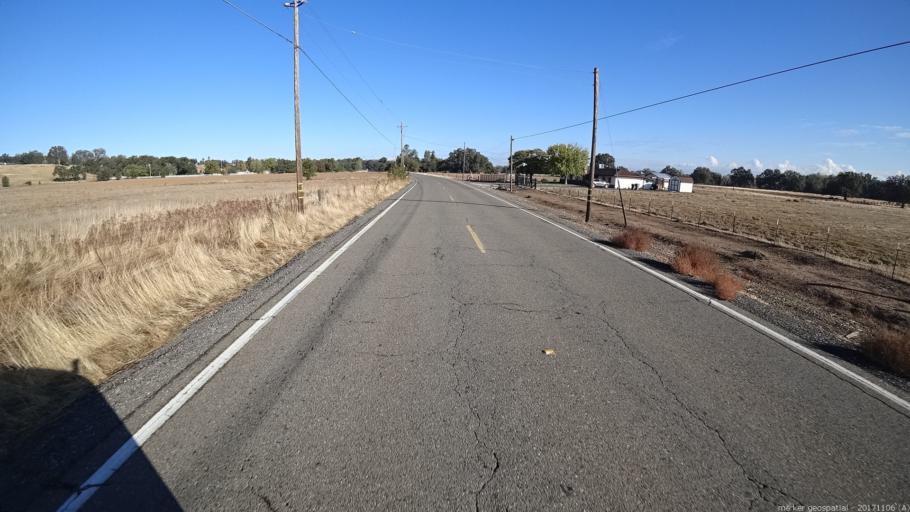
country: US
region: California
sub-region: Shasta County
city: Anderson
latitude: 40.4886
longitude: -122.2389
